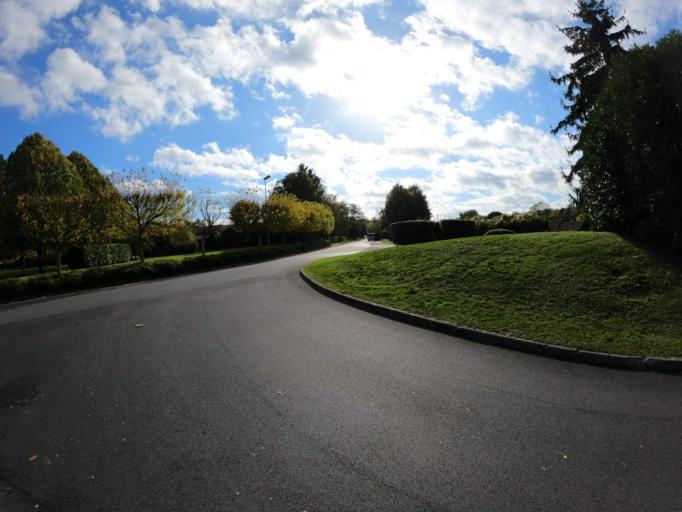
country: FR
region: Ile-de-France
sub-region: Departement de Seine-et-Marne
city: Esbly
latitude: 48.8942
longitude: 2.8103
